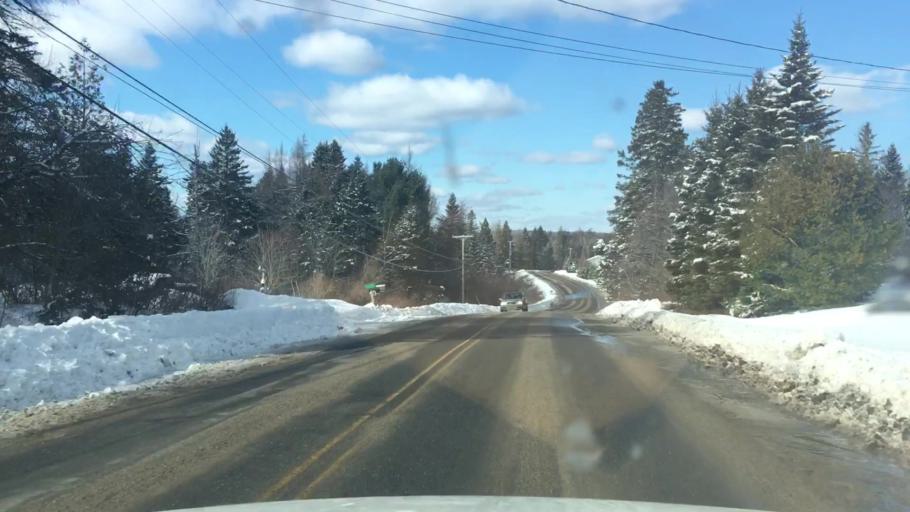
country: US
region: Maine
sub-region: Washington County
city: Machias
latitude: 44.6907
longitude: -67.4655
